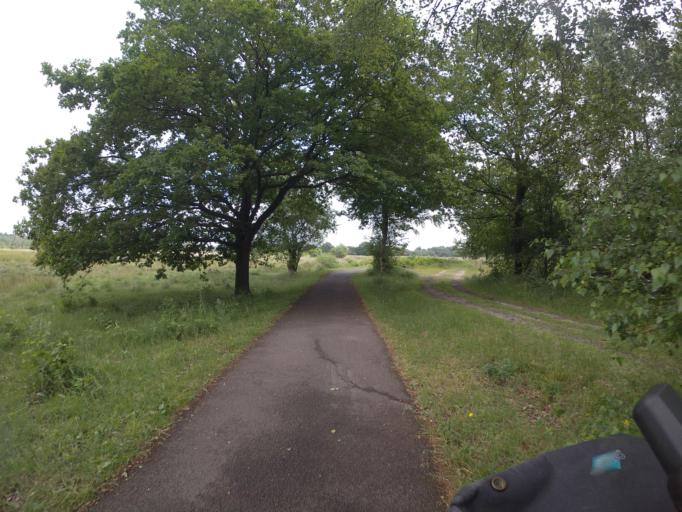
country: NL
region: Drenthe
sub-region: Gemeente Hoogeveen
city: Hoogeveen
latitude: 52.8345
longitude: 6.4904
